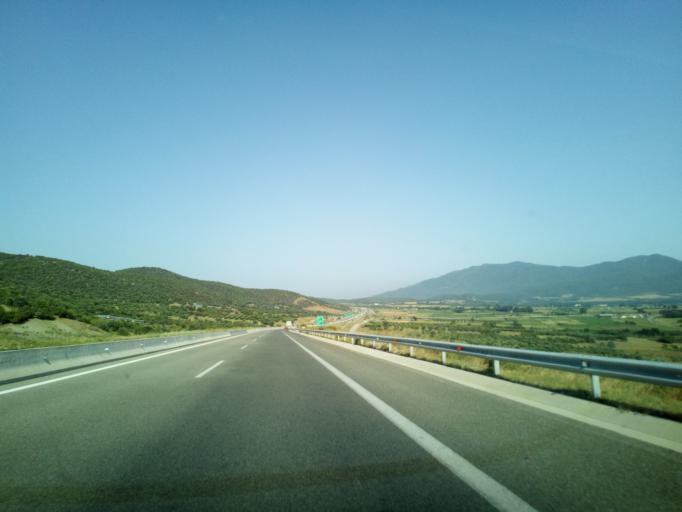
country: GR
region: Central Macedonia
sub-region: Nomos Thessalonikis
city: Stavros
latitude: 40.6802
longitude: 23.5727
